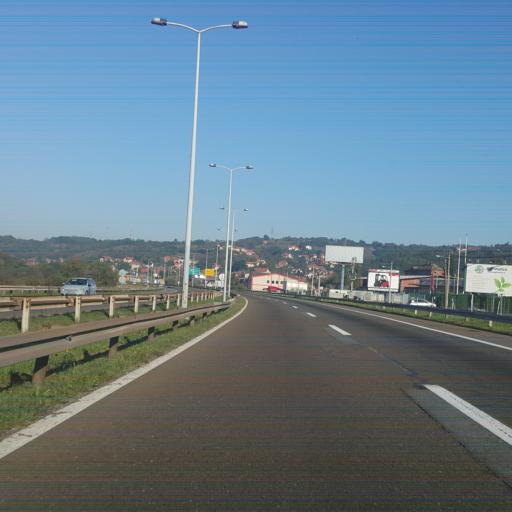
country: RS
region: Central Serbia
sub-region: Belgrade
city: Grocka
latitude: 44.6706
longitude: 20.6073
